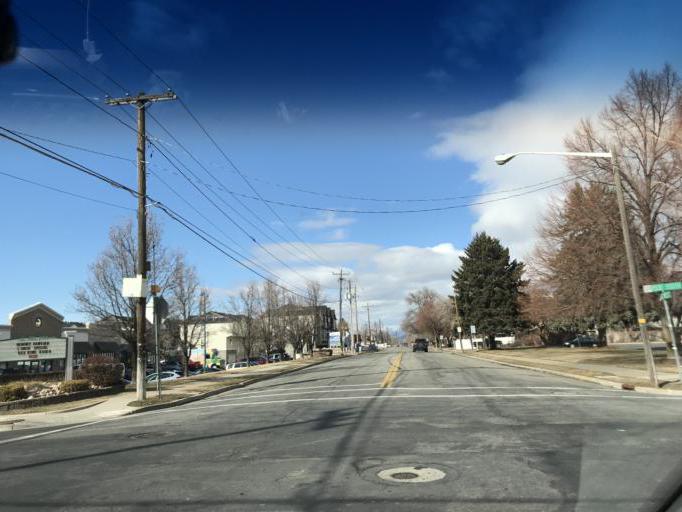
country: US
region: Utah
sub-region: Davis County
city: Woods Cross
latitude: 40.8747
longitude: -111.9021
